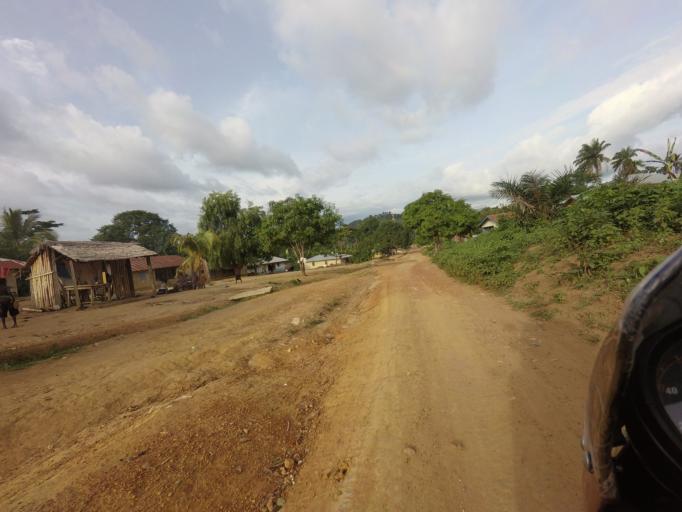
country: SL
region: Eastern Province
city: Jojoima
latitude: 7.8733
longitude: -10.7914
